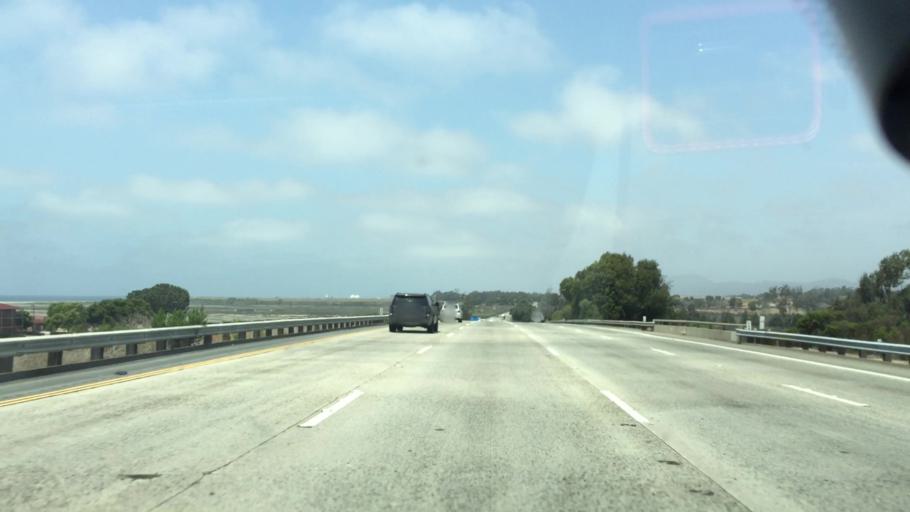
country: US
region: California
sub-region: San Diego County
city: Camp Pendleton South
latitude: 33.2271
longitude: -117.3963
